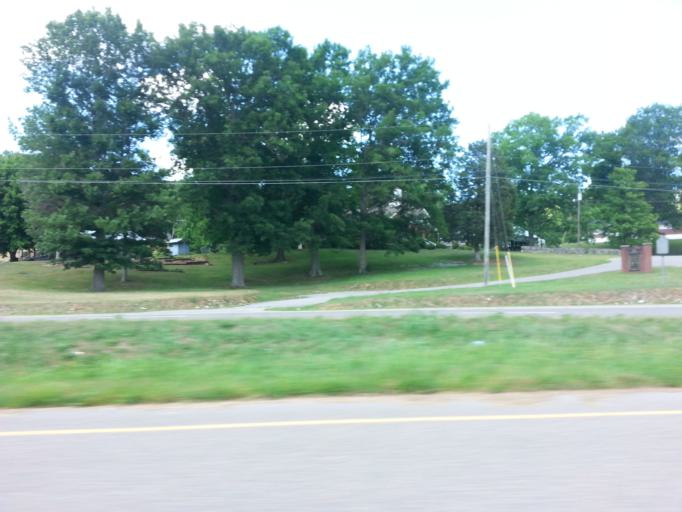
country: US
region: Virginia
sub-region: Lee County
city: Jonesville
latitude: 36.6816
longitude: -83.1441
